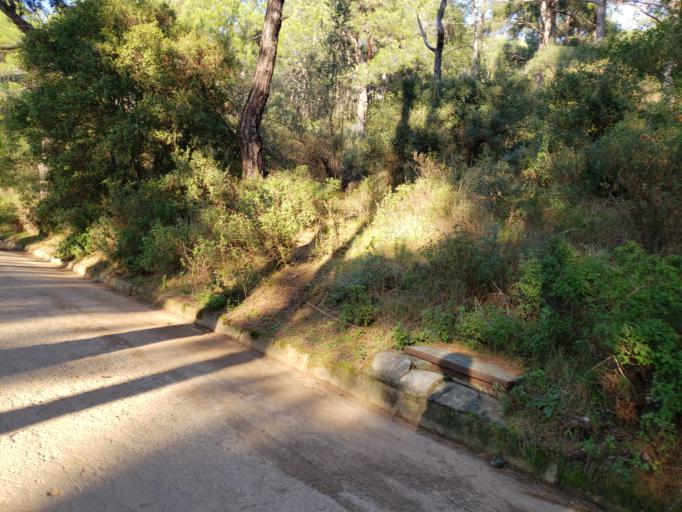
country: TR
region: Istanbul
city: Adalan
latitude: 40.8717
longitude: 29.0933
